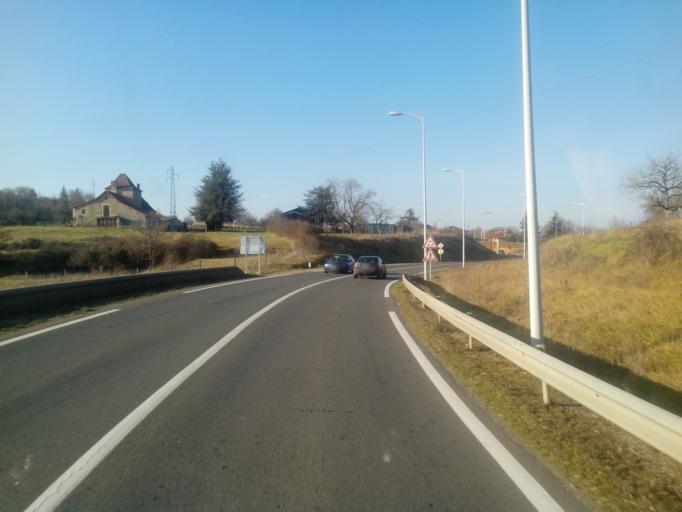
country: FR
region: Midi-Pyrenees
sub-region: Departement du Lot
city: Figeac
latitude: 44.5947
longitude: 2.0573
